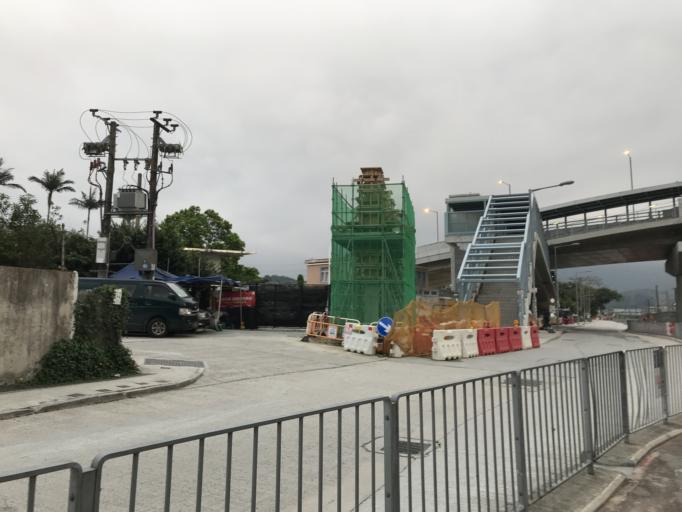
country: HK
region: Tai Po
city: Tai Po
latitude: 22.4756
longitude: 114.1546
